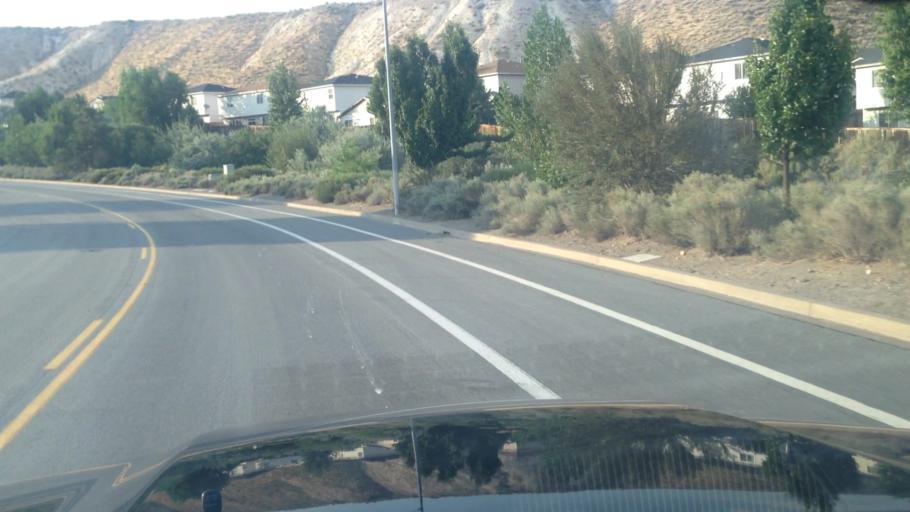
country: US
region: Nevada
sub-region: Washoe County
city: Mogul
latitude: 39.5372
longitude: -119.8819
